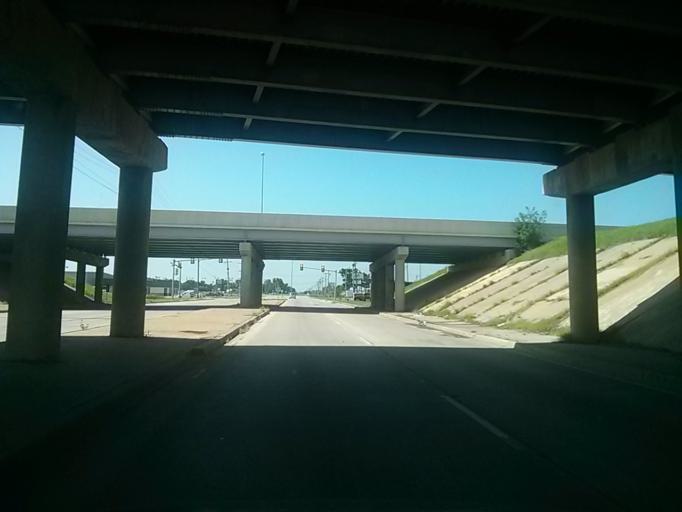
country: US
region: Oklahoma
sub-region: Tulsa County
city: Owasso
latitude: 36.1647
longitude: -95.8688
